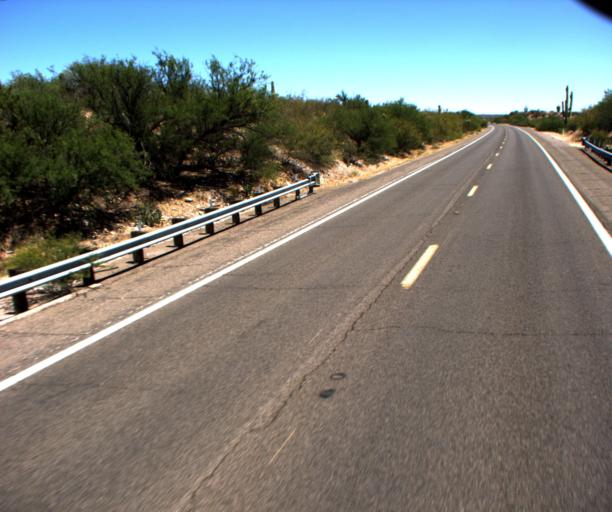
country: US
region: Arizona
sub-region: Pinal County
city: Mammoth
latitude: 32.8212
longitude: -110.6942
